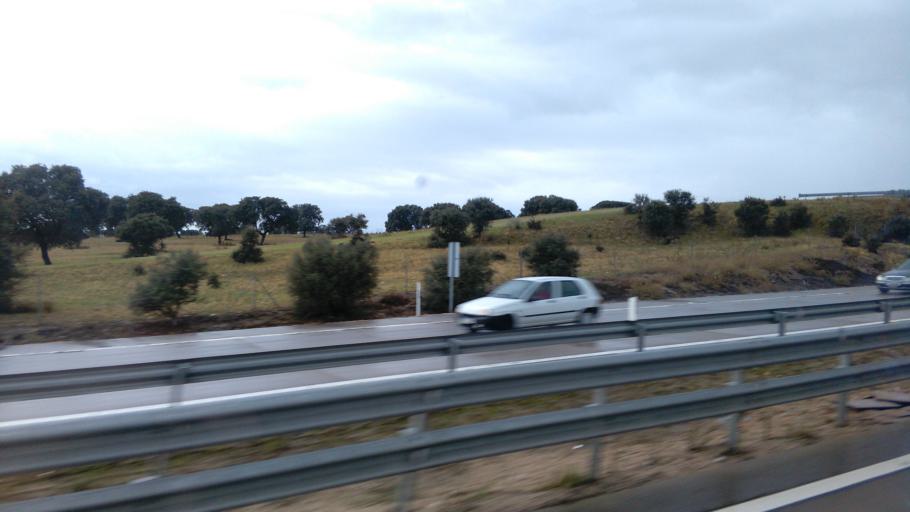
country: ES
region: Castille-La Mancha
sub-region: Province of Toledo
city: Cervera de los Montes
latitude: 40.0157
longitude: -4.7842
